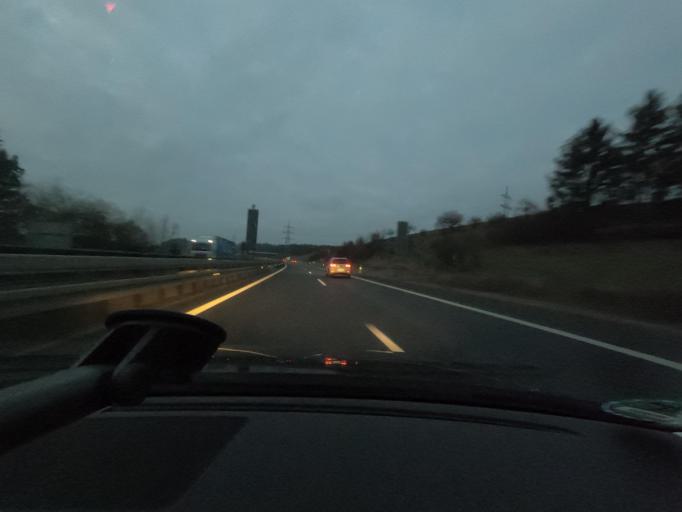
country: DE
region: Bavaria
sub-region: Upper Franconia
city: Rodental
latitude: 50.2410
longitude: 11.0469
